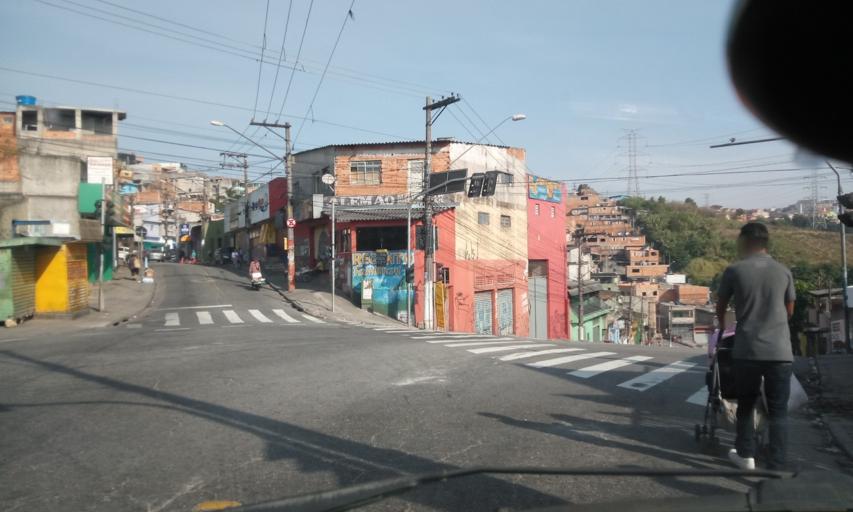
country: BR
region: Sao Paulo
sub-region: Santo Andre
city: Santo Andre
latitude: -23.7042
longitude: -46.5185
